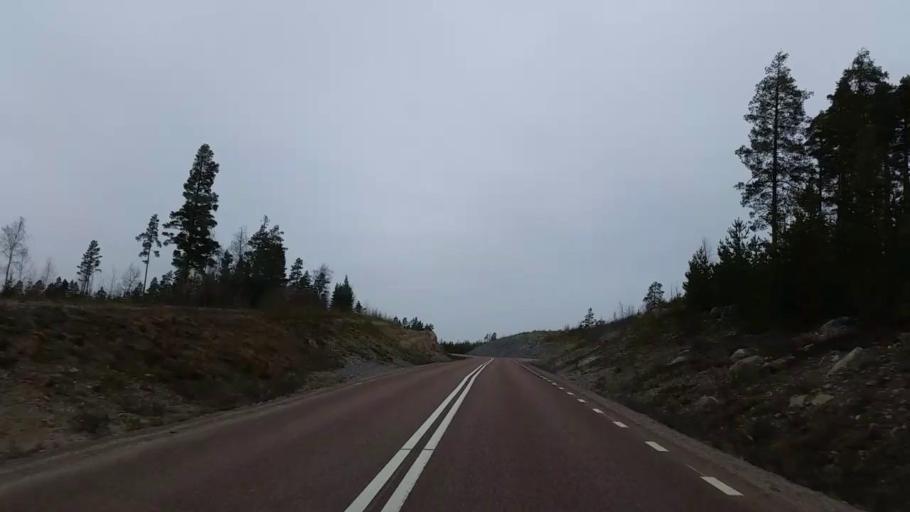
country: SE
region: Gaevleborg
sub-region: Ovanakers Kommun
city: Edsbyn
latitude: 61.2324
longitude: 15.8838
